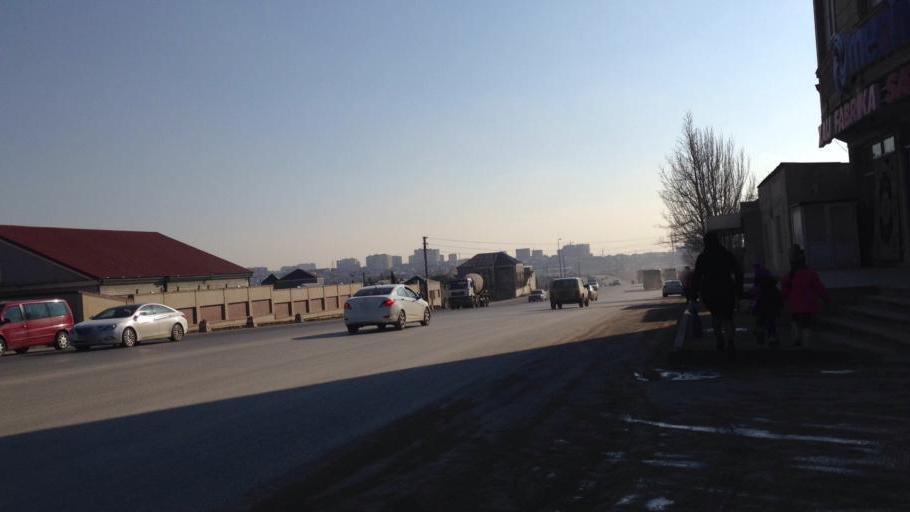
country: AZ
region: Baki
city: Sabuncu
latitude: 40.4442
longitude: 49.9338
